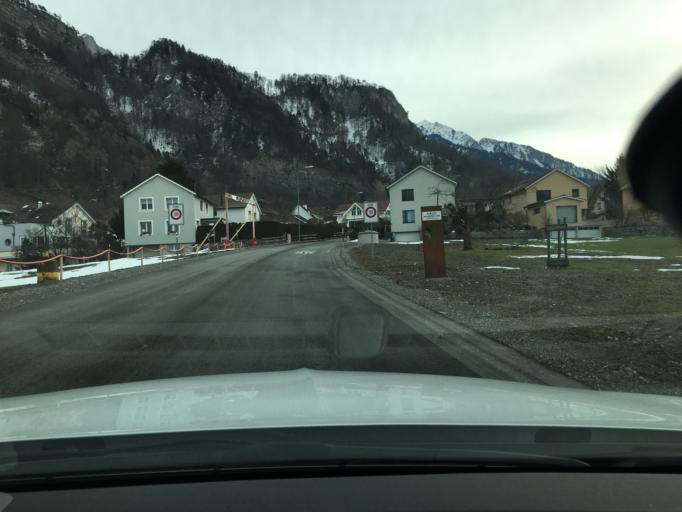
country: CH
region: Saint Gallen
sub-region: Wahlkreis Sarganserland
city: Bad Ragaz
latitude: 47.0271
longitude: 9.5090
